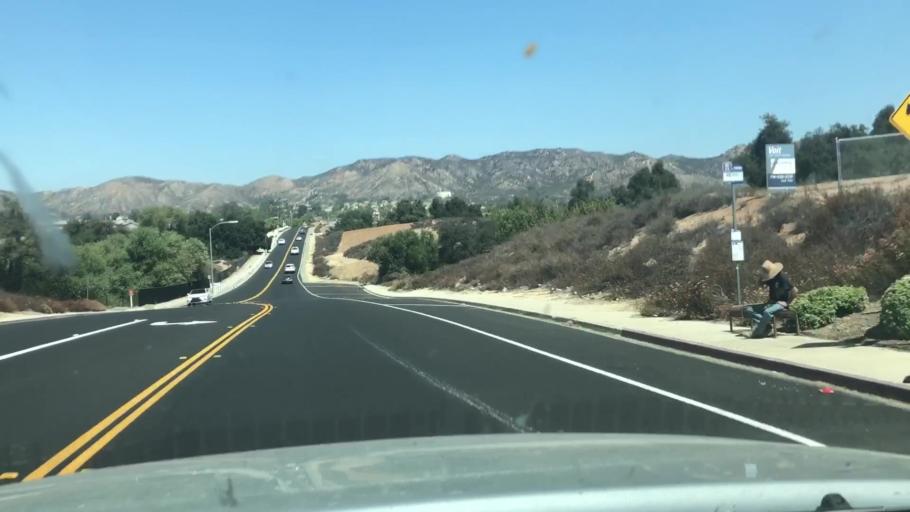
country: US
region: California
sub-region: Riverside County
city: Wildomar
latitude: 33.5930
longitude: -117.2368
